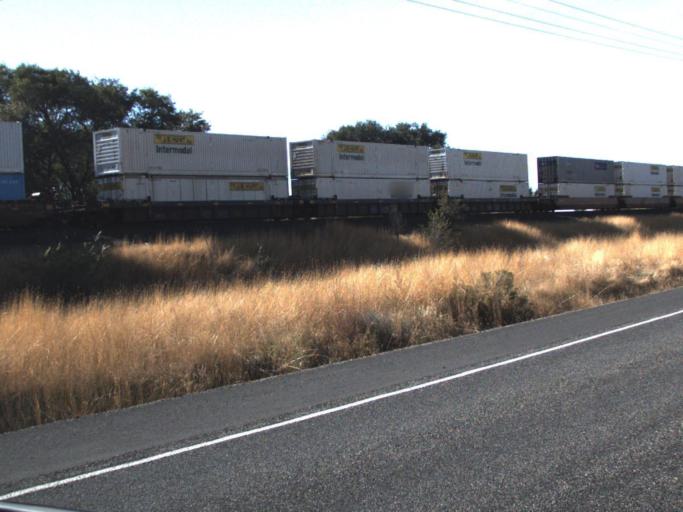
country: US
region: Washington
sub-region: Benton County
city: Finley
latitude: 46.1591
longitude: -119.0376
